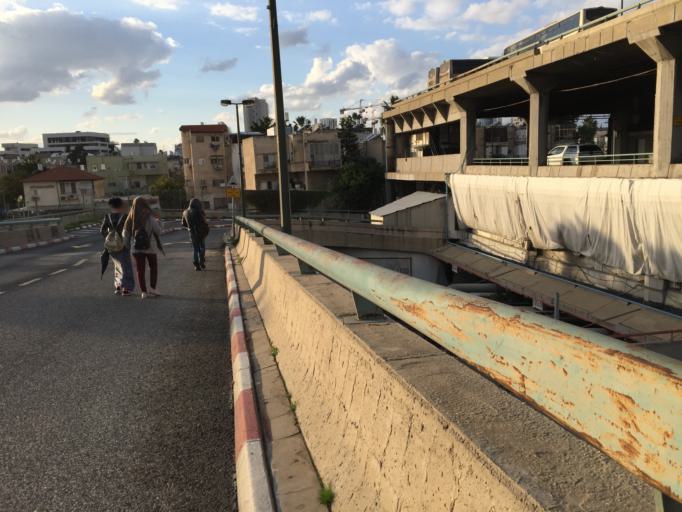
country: IL
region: Tel Aviv
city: Tel Aviv
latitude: 32.0556
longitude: 34.7787
